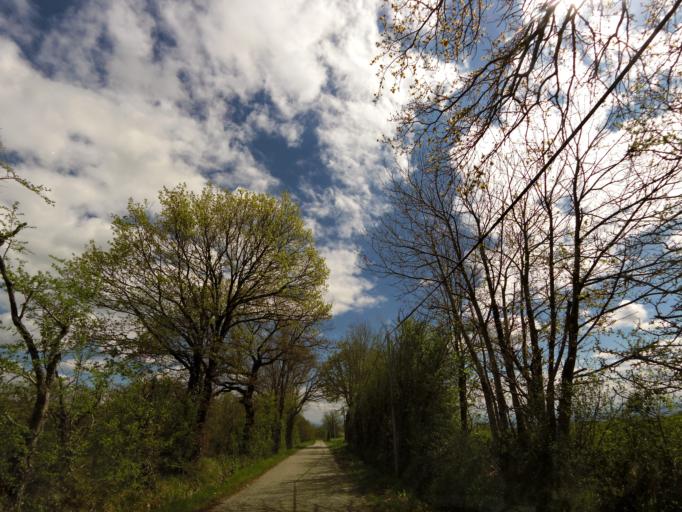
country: FR
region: Midi-Pyrenees
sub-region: Departement du Tarn
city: Soreze
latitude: 43.3718
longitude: 2.0648
